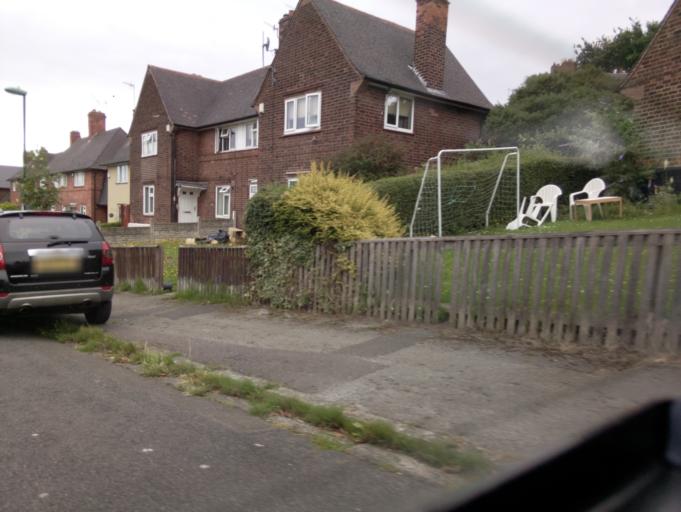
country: GB
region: England
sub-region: Nottinghamshire
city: Arnold
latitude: 52.9865
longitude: -1.1508
